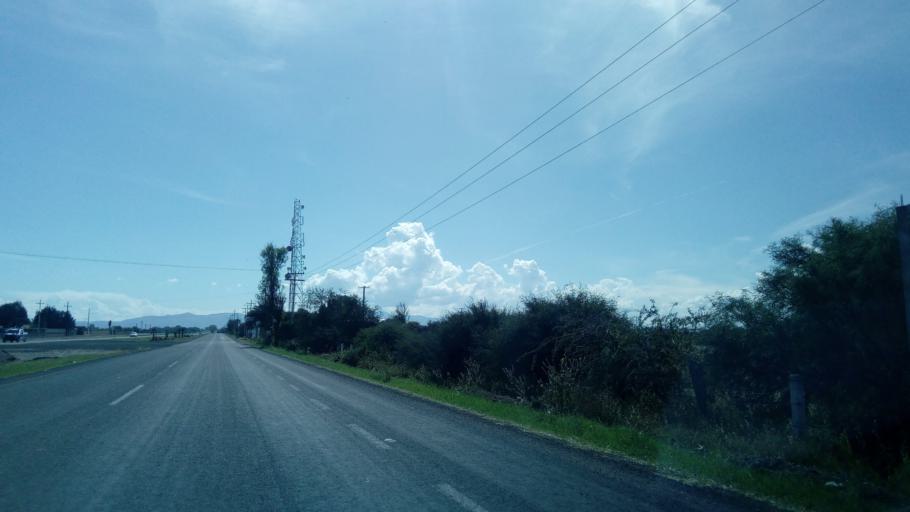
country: MX
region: Durango
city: Victoria de Durango
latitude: 24.0824
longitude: -104.5580
